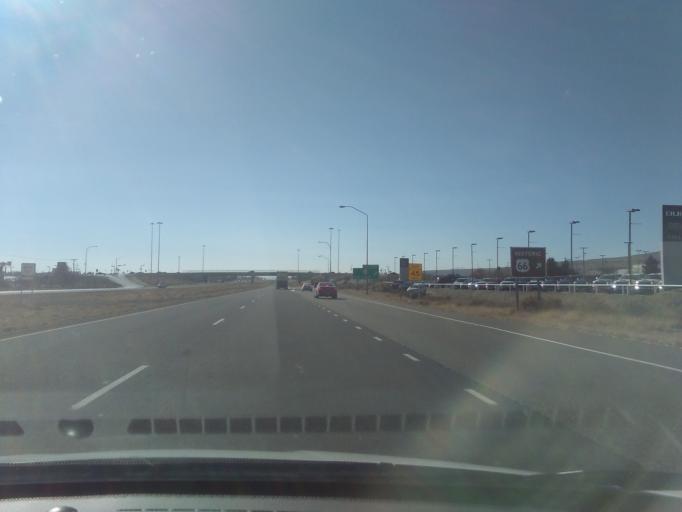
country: US
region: New Mexico
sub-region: Valencia County
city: Los Lunas
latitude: 34.8186
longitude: -106.7596
